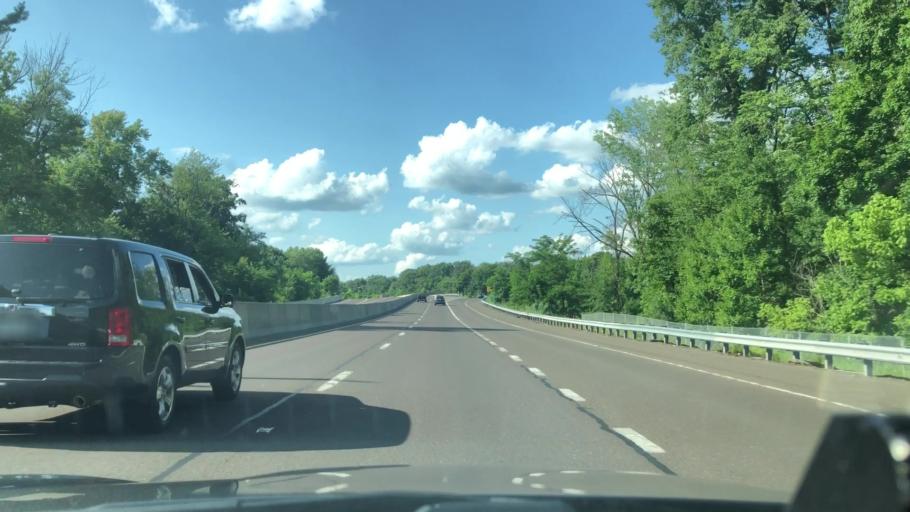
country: US
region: Pennsylvania
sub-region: Montgomery County
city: Fort Washington
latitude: 40.1579
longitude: -75.2011
